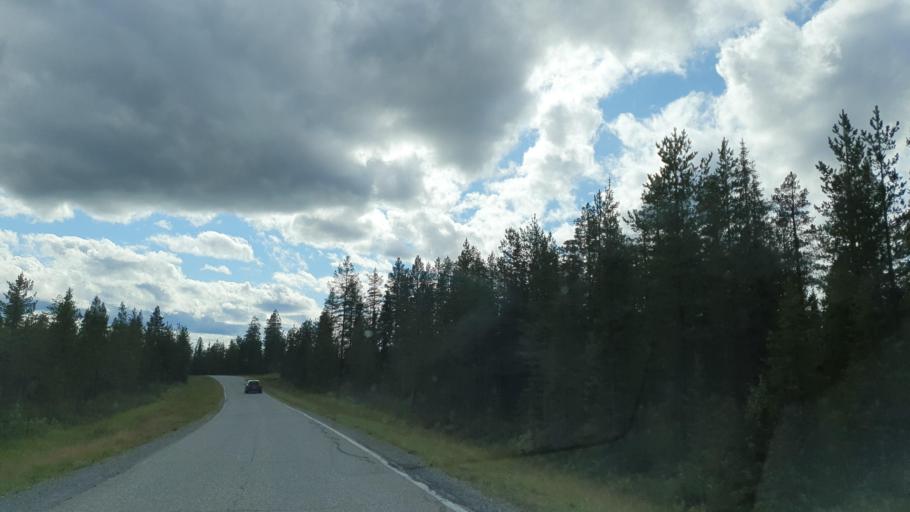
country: FI
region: Lapland
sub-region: Tunturi-Lappi
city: Muonio
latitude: 67.7240
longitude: 24.0751
